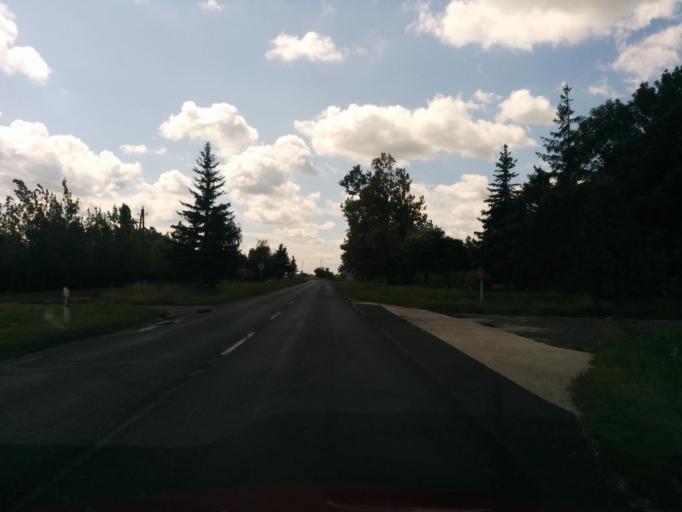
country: HU
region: Komarom-Esztergom
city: Komarom
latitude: 47.7024
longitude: 18.1062
